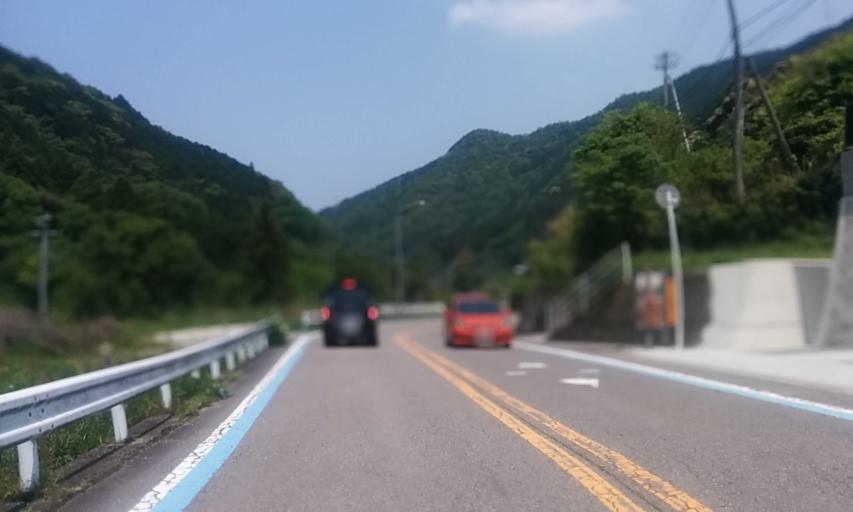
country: JP
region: Ehime
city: Niihama
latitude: 33.9096
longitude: 133.3086
